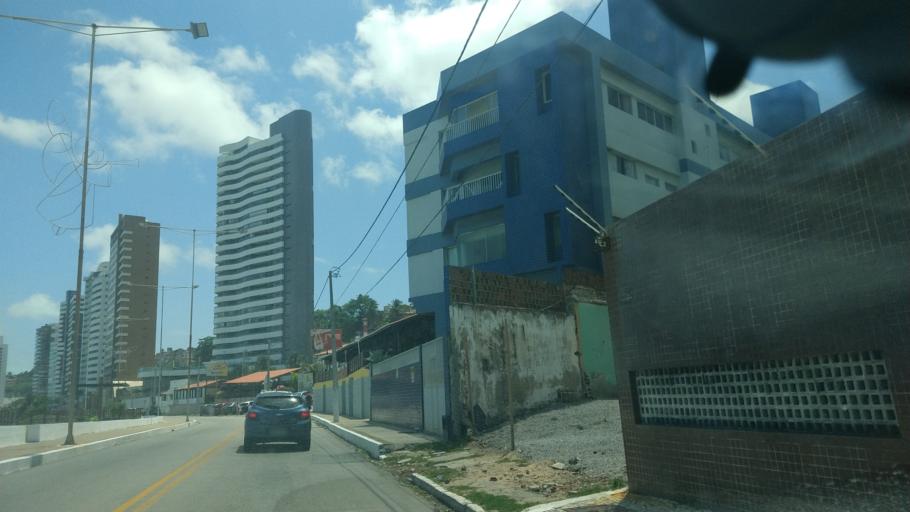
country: BR
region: Rio Grande do Norte
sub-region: Natal
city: Natal
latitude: -5.7853
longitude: -35.1905
